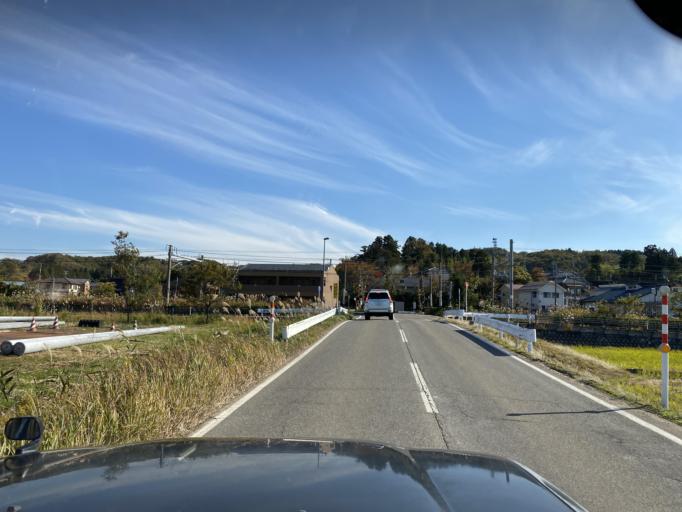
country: JP
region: Niigata
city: Niitsu-honcho
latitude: 37.7533
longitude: 139.0978
